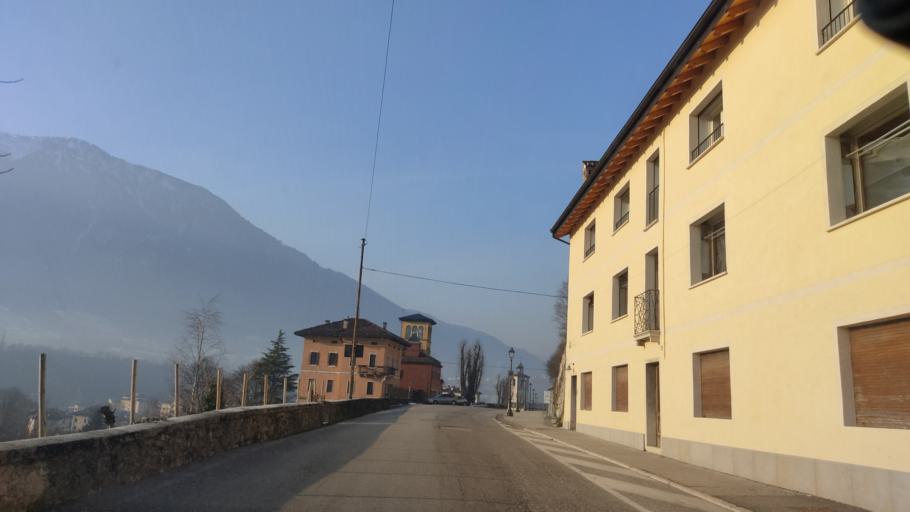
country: IT
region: Veneto
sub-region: Provincia di Belluno
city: Feltre
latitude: 46.0189
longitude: 11.9132
